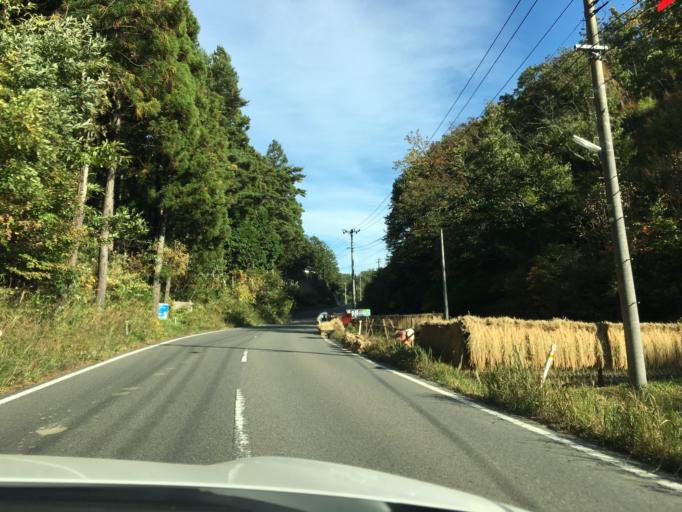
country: JP
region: Fukushima
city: Miharu
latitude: 37.3582
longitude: 140.5359
